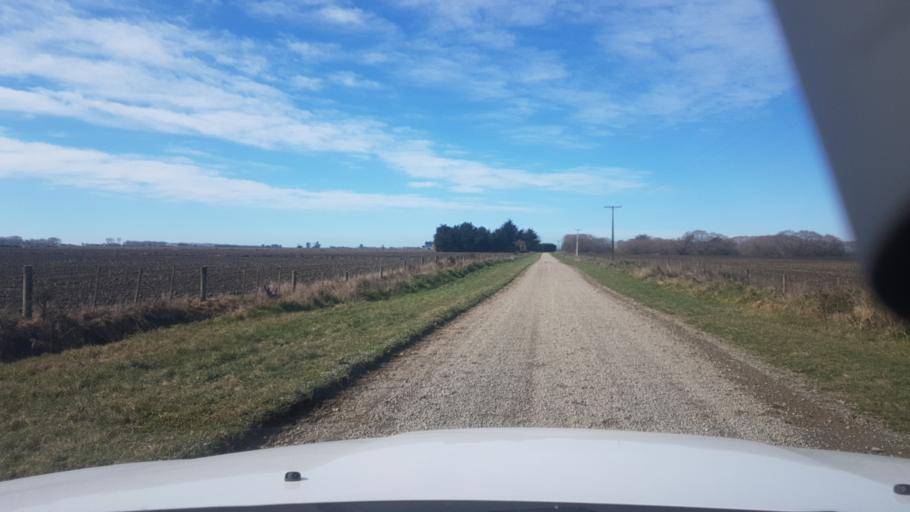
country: NZ
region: Canterbury
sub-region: Timaru District
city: Timaru
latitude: -44.2612
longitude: 171.3409
